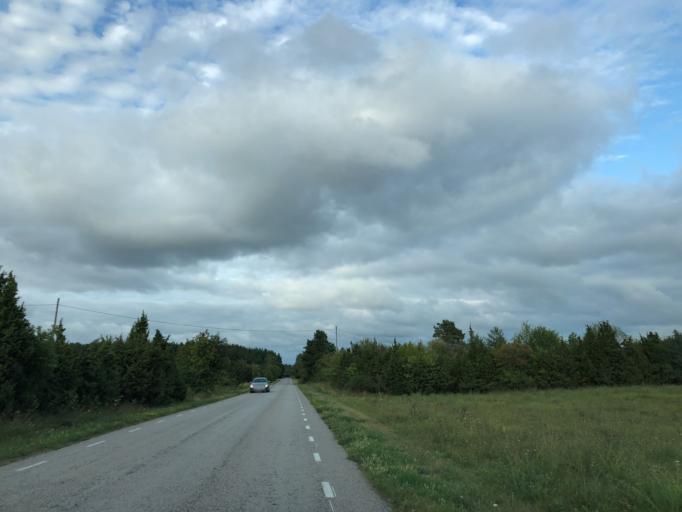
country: EE
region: Hiiumaa
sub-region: Kaerdla linn
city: Kardla
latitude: 58.7863
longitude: 22.7919
